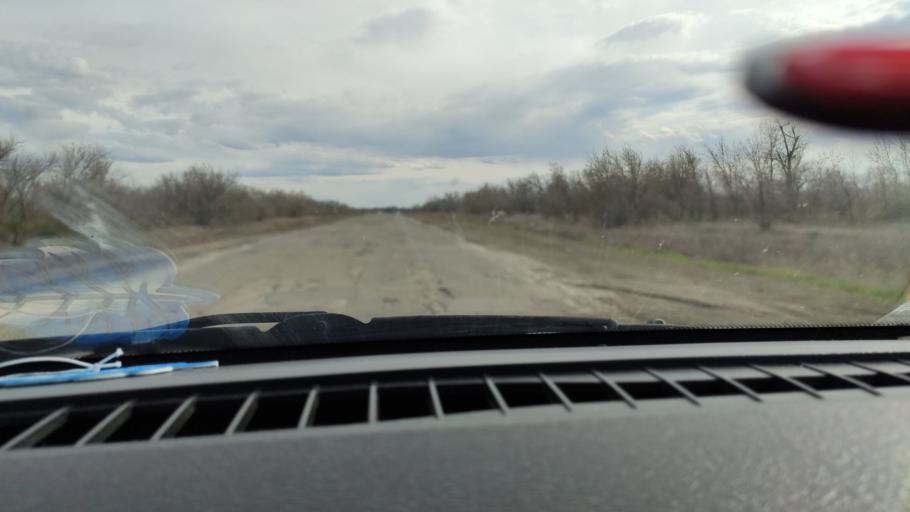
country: RU
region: Saratov
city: Rovnoye
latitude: 50.9656
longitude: 46.1169
